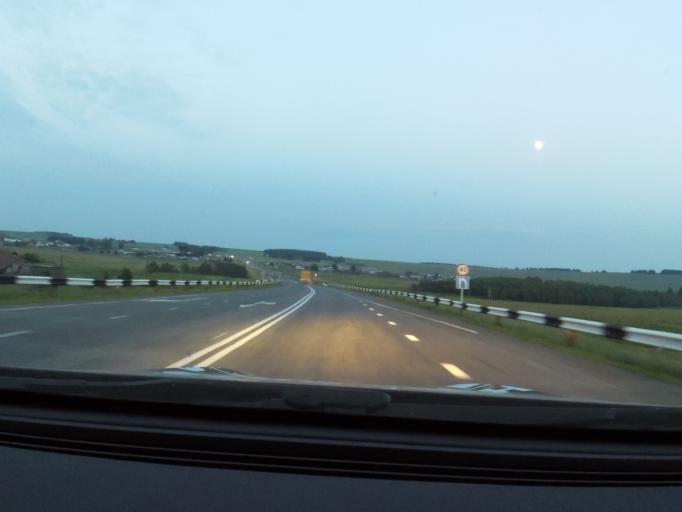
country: RU
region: Sverdlovsk
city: Sarana
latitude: 56.1335
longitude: 58.0062
